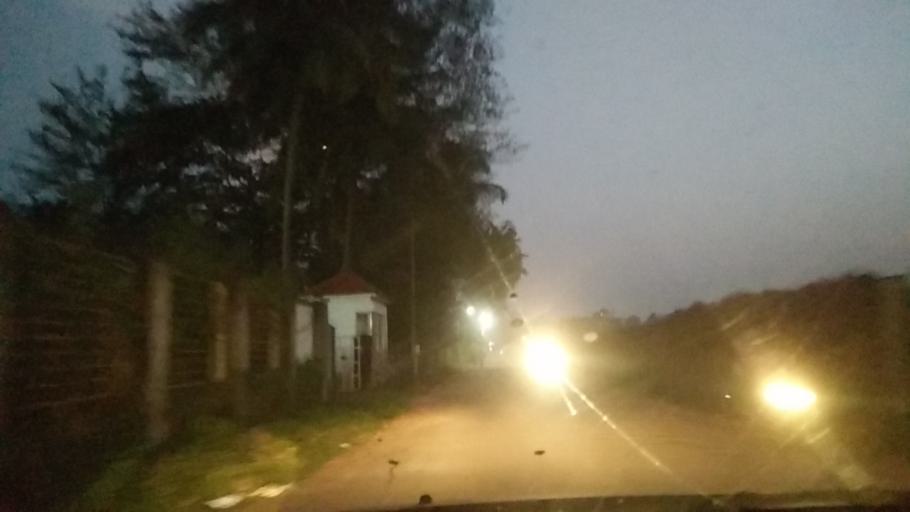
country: IN
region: Goa
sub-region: South Goa
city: Madgaon
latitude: 15.2671
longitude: 73.9647
